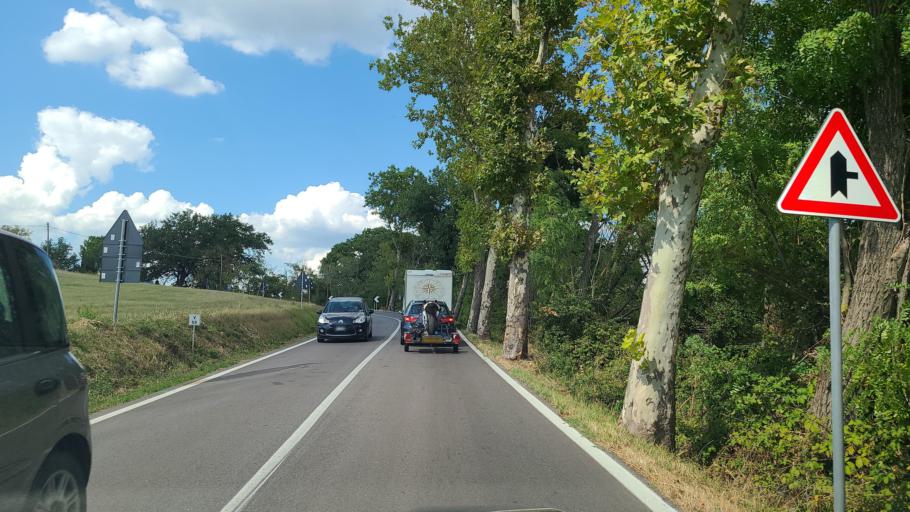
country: IT
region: Tuscany
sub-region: Provincia di Siena
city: Casole d'Elsa
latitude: 43.4042
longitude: 11.0242
